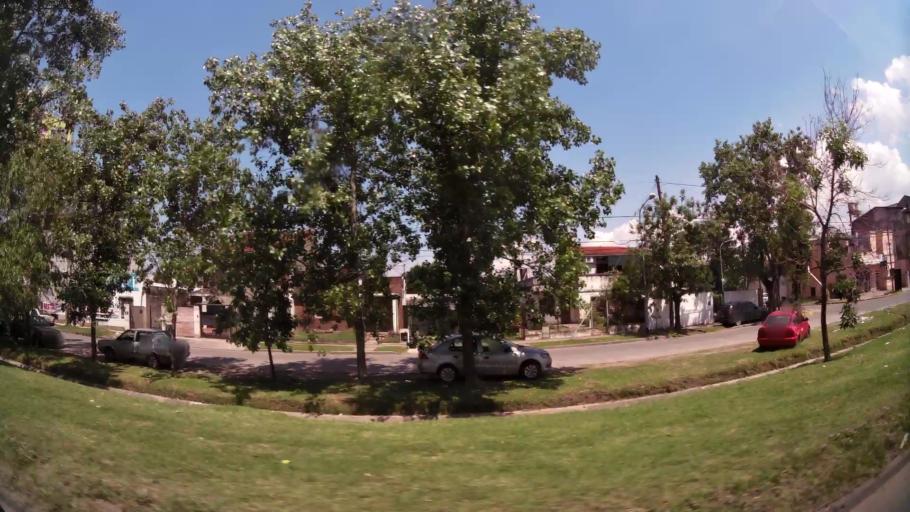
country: AR
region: Buenos Aires
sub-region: Partido de Tigre
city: Tigre
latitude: -34.4457
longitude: -58.6001
